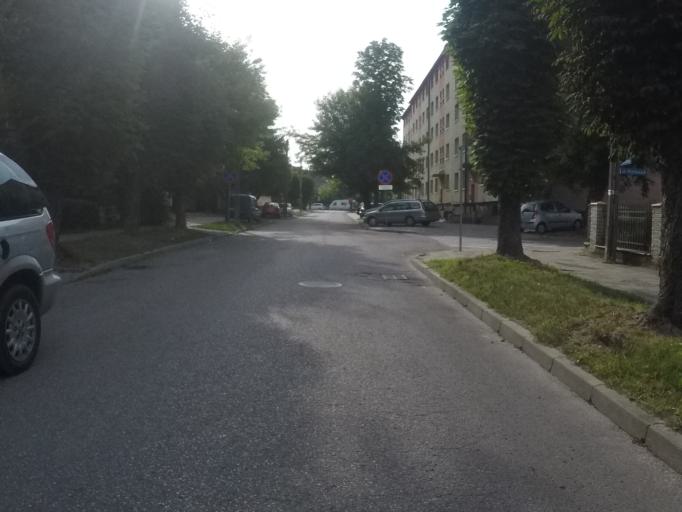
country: PL
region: Podlasie
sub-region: Powiat augustowski
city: Augustow
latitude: 53.8458
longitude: 22.9957
